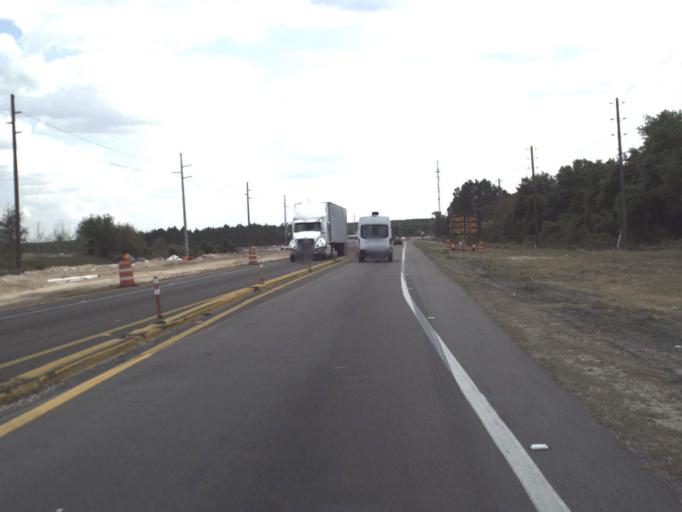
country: US
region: Florida
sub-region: Lake County
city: Clermont
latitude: 28.4822
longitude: -81.7151
